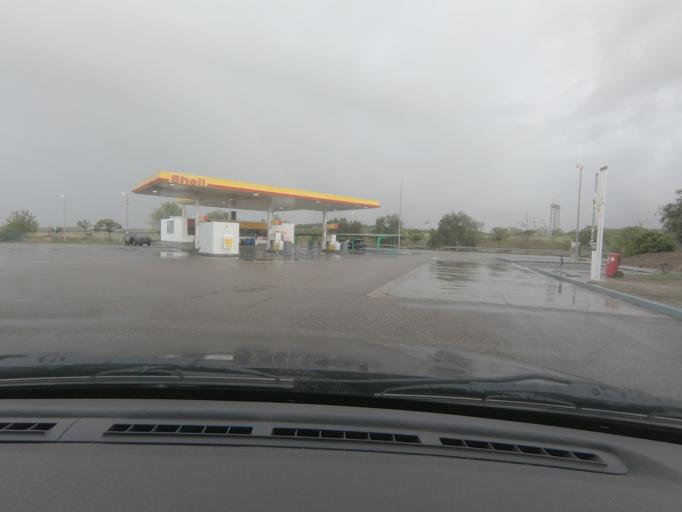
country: ES
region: Extremadura
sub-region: Provincia de Badajoz
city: Talavera La Real
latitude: 38.8655
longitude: -6.8118
